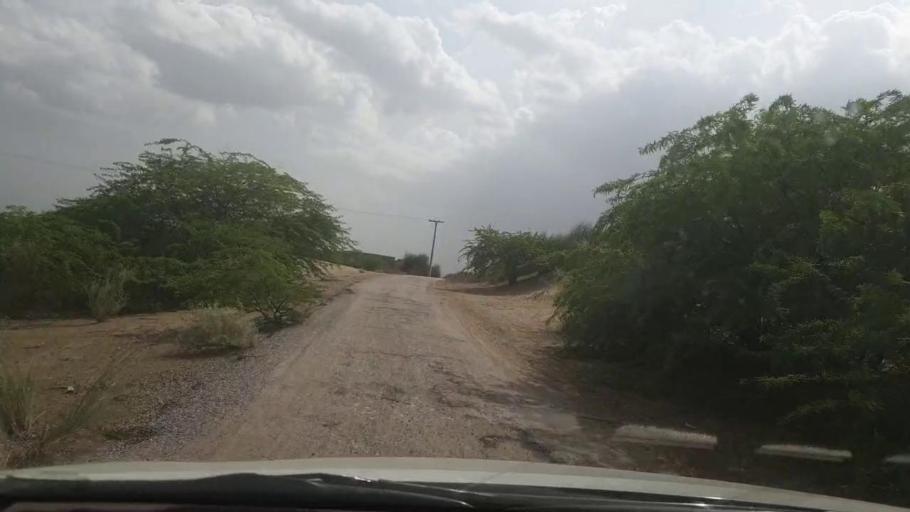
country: PK
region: Sindh
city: Kot Diji
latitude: 27.3411
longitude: 69.0190
